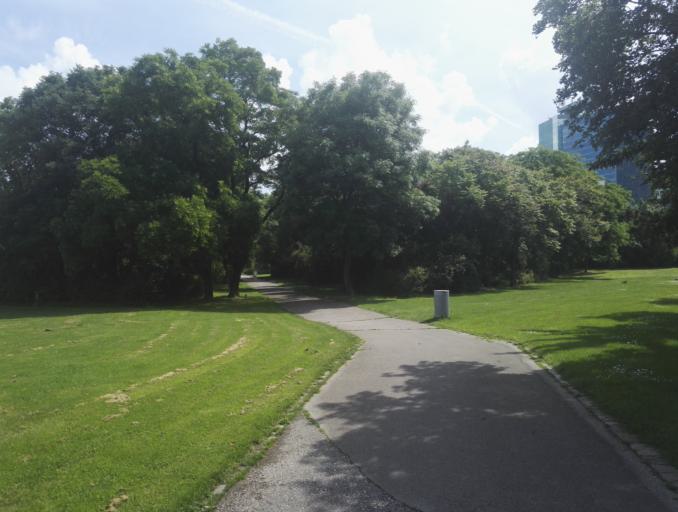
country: AT
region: Vienna
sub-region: Wien Stadt
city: Vienna
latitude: 48.2370
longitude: 16.4084
